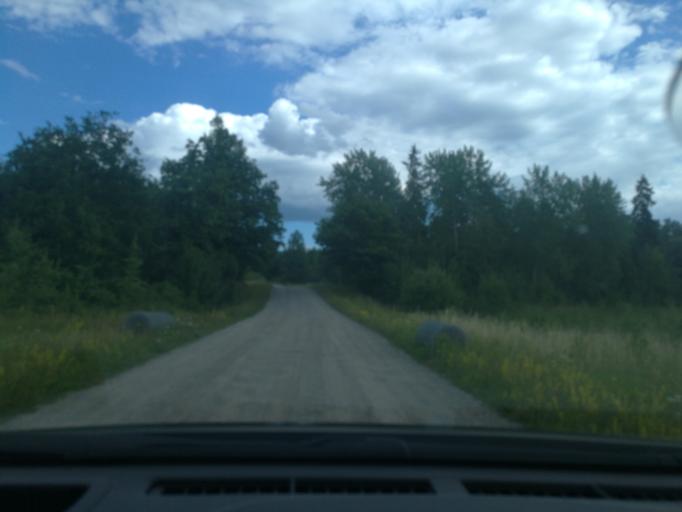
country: SE
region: Soedermanland
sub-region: Strangnas Kommun
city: Strangnas
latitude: 59.3926
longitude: 16.9785
